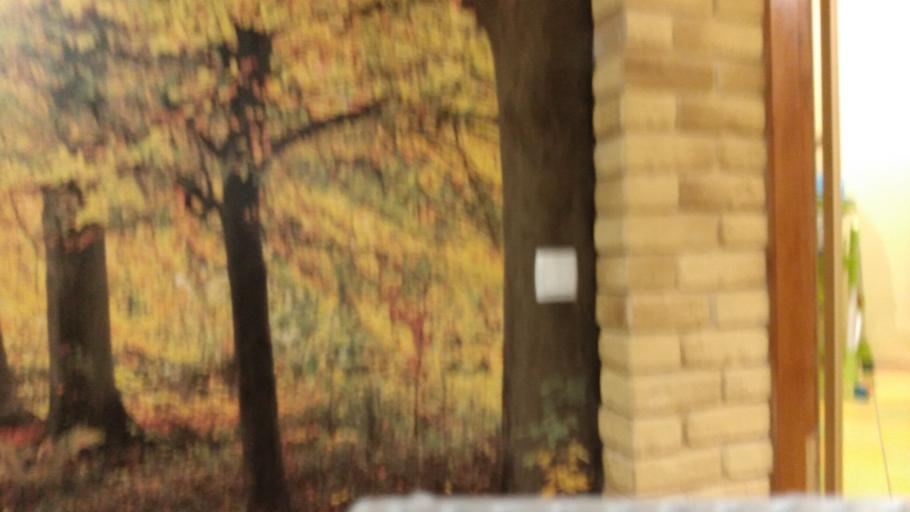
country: RU
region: Vologda
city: Babayevo
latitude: 59.3744
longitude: 35.9919
